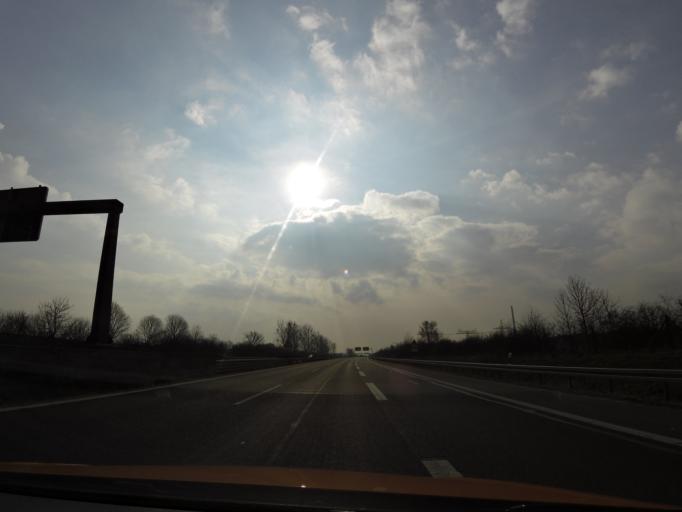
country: DE
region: Brandenburg
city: Ludwigsfelde
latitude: 52.3251
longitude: 13.2867
